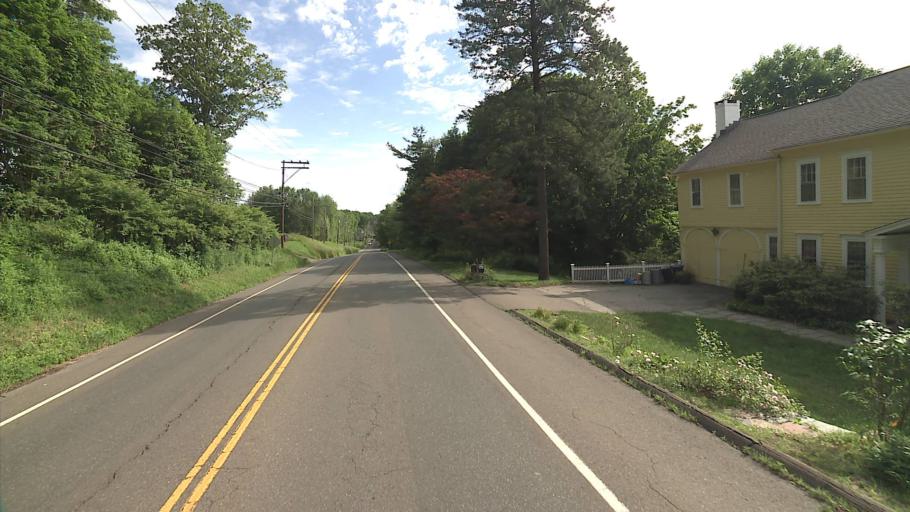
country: US
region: Connecticut
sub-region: New Haven County
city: Woodbridge
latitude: 41.4169
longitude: -72.9985
